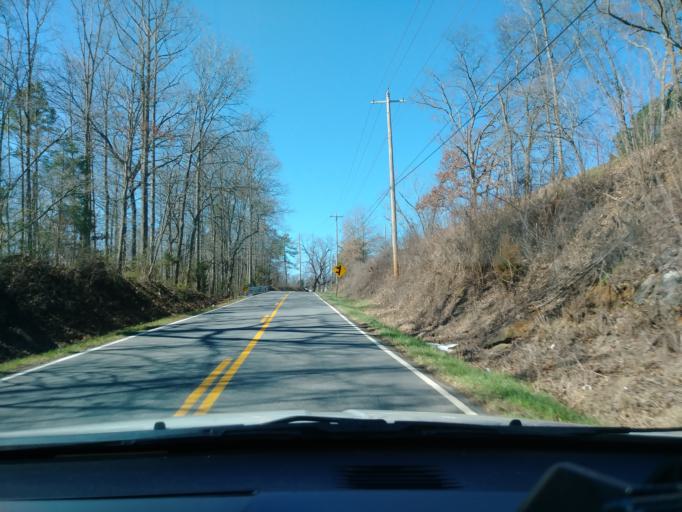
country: US
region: Tennessee
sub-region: Cocke County
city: Newport
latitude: 35.9980
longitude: -83.0840
